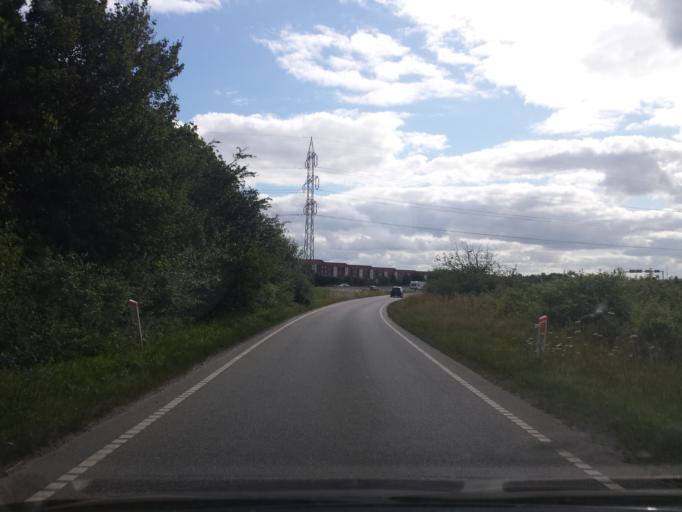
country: DK
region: South Denmark
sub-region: Sonderborg Kommune
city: Sonderborg
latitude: 54.9248
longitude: 9.7780
